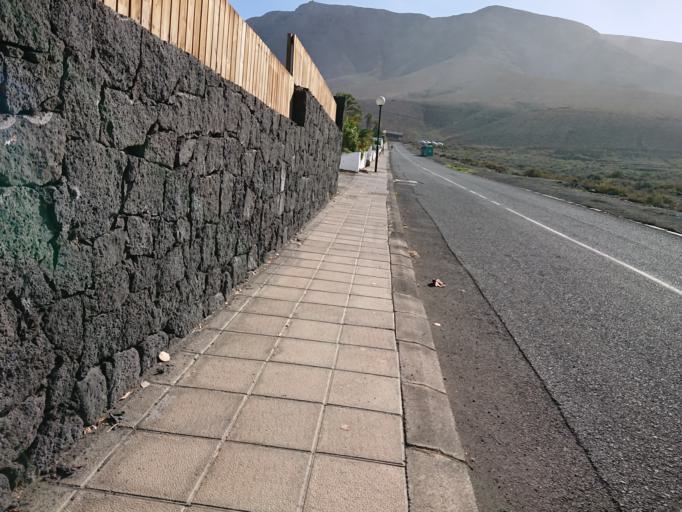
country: ES
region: Canary Islands
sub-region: Provincia de Las Palmas
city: Teguise
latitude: 29.1124
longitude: -13.5475
